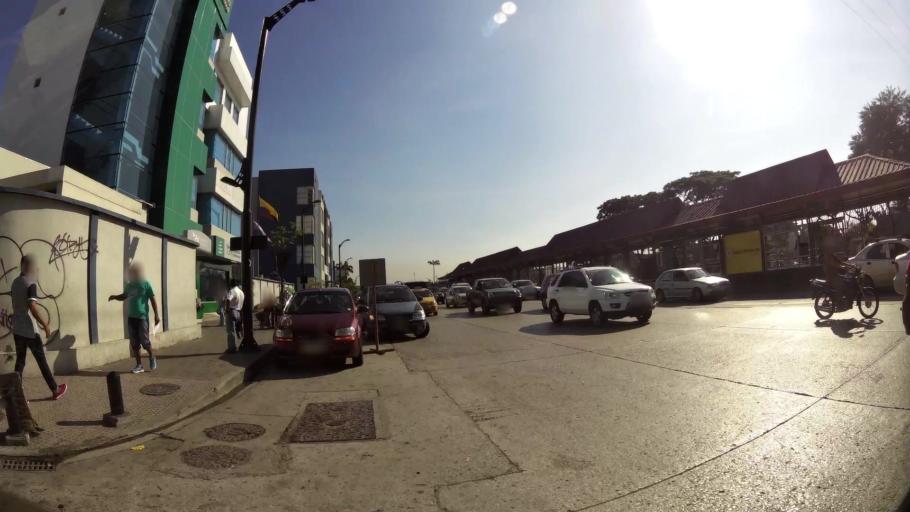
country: EC
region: Guayas
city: Guayaquil
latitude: -2.1775
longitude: -79.8921
